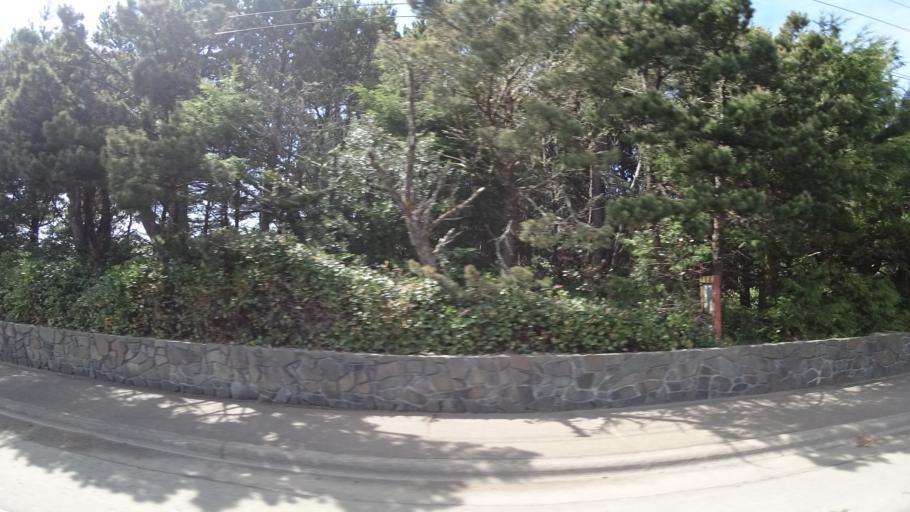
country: US
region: Oregon
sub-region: Lincoln County
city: Lincoln Beach
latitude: 44.8533
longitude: -124.0425
